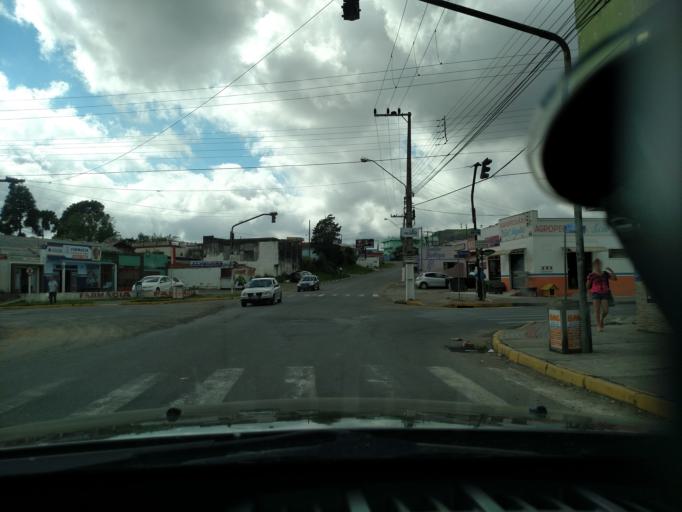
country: BR
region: Santa Catarina
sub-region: Lages
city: Lages
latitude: -27.8123
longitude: -50.2904
